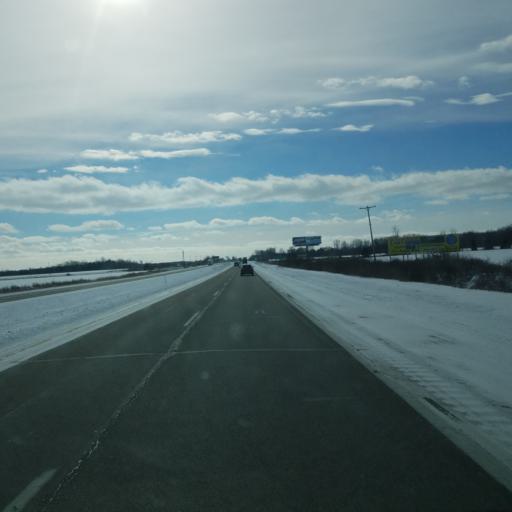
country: US
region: Michigan
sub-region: Gratiot County
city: Ithaca
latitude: 43.2224
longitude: -84.5635
